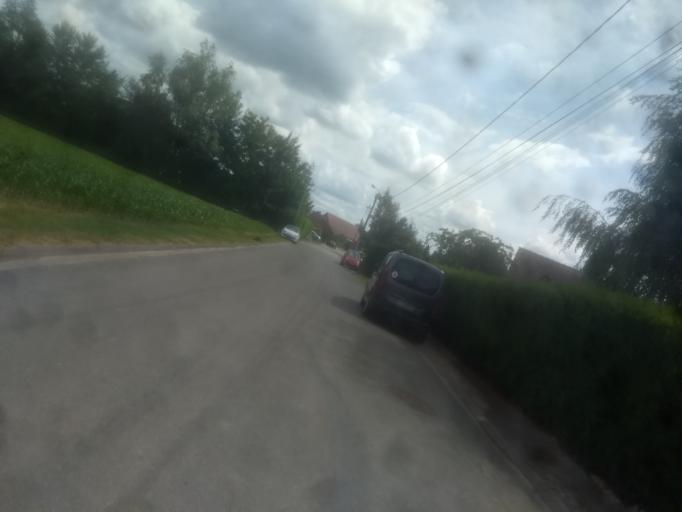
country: FR
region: Nord-Pas-de-Calais
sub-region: Departement du Pas-de-Calais
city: Duisans
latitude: 50.3156
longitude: 2.6492
